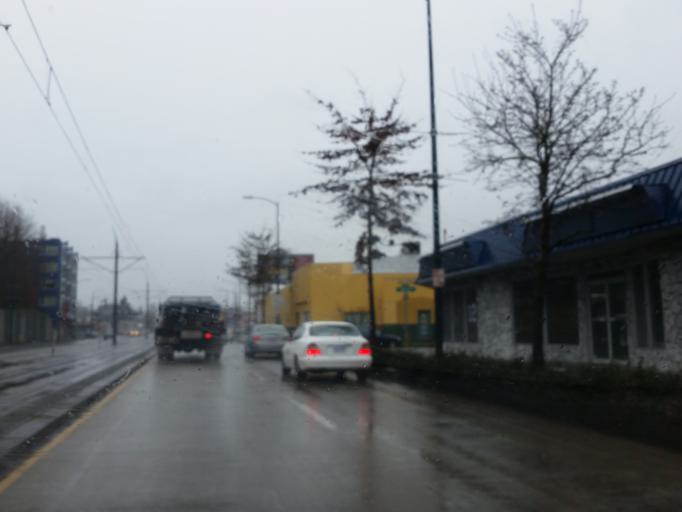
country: US
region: Washington
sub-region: King County
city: Riverton
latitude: 47.5493
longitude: -122.2871
